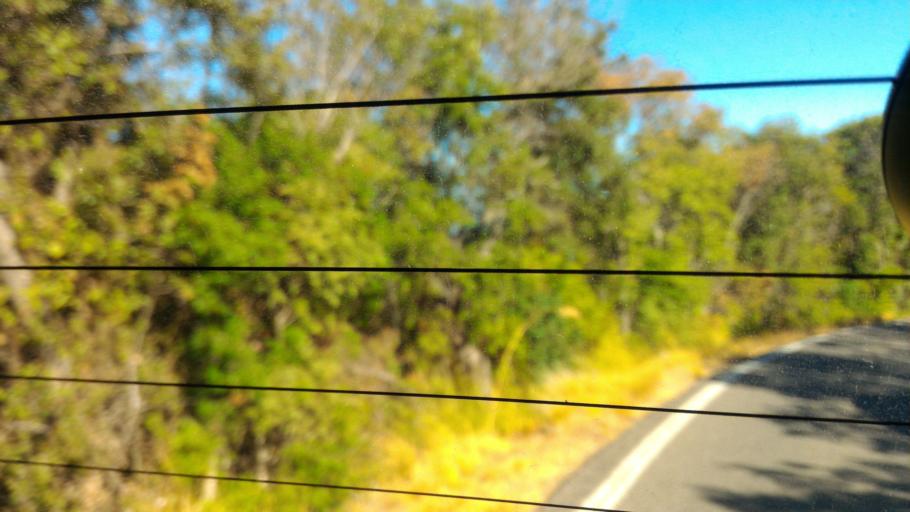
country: IT
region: Tuscany
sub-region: Provincia di Grosseto
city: Porto Ercole
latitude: 42.4219
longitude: 11.1661
